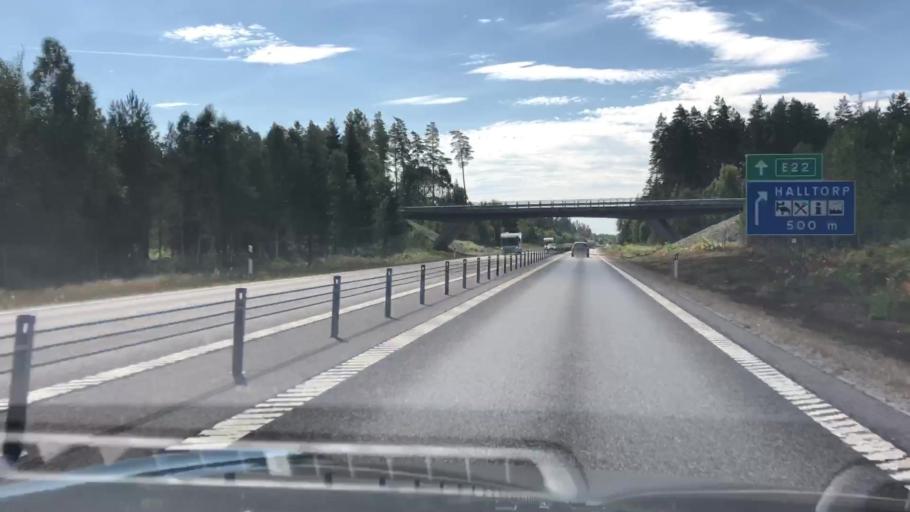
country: SE
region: Kalmar
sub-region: Torsas Kommun
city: Torsas
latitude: 56.5128
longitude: 16.0860
